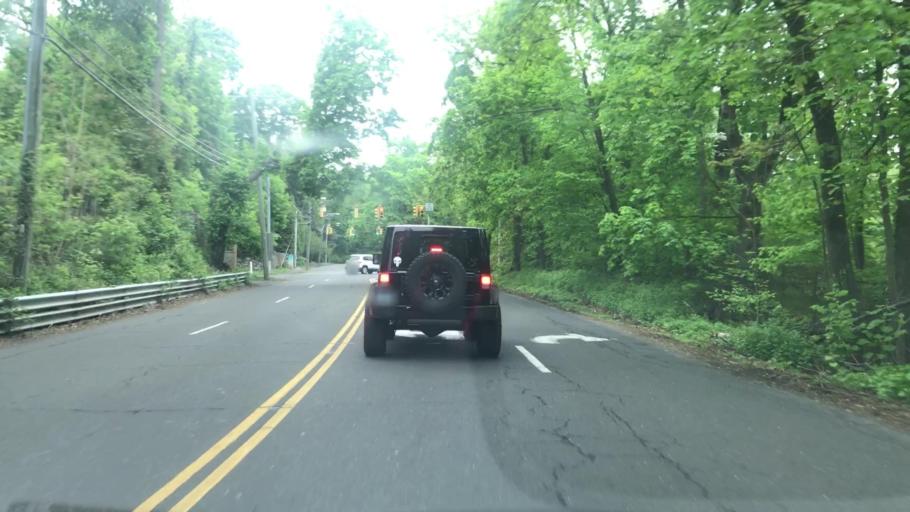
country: US
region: Connecticut
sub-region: Fairfield County
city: Stamford
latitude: 41.0635
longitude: -73.5583
